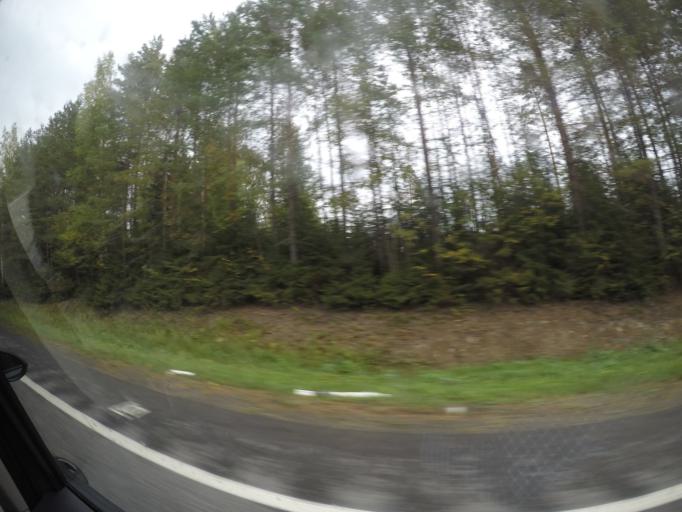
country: FI
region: Haeme
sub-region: Haemeenlinna
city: Parola
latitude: 61.1472
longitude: 24.4129
